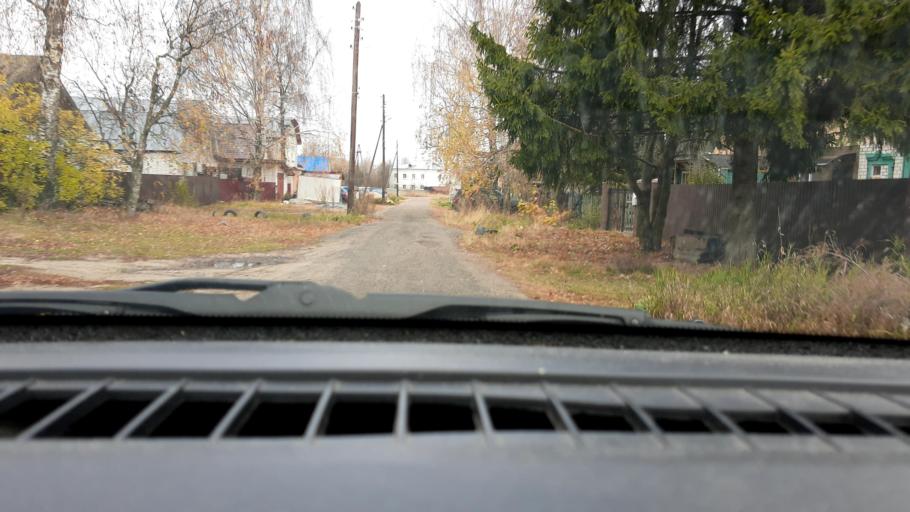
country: RU
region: Nizjnij Novgorod
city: Lukino
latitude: 56.4031
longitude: 43.7200
